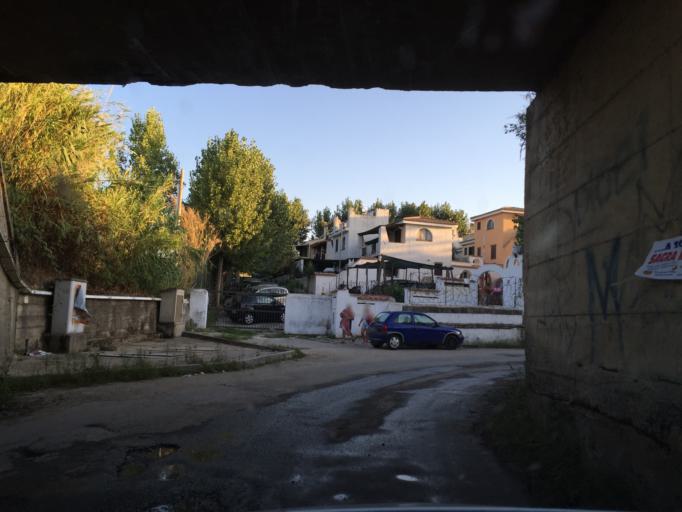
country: IT
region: Calabria
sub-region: Provincia di Vibo-Valentia
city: Briatico
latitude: 38.7207
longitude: 16.0564
